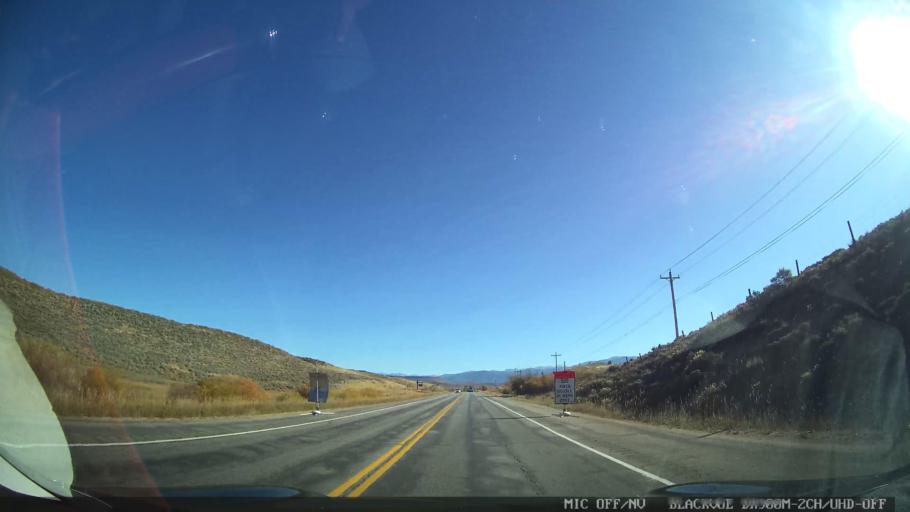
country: US
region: Colorado
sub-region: Grand County
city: Granby
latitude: 40.0982
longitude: -105.9523
